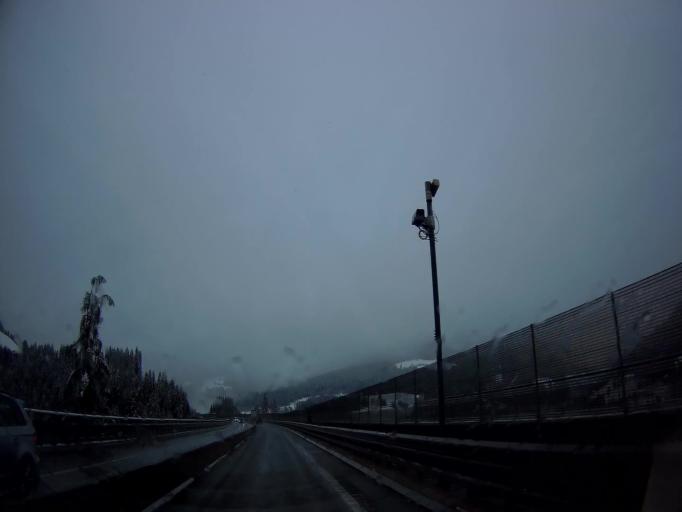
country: AT
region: Salzburg
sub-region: Politischer Bezirk Sankt Johann im Pongau
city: Huttau
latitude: 47.4164
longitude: 13.3174
